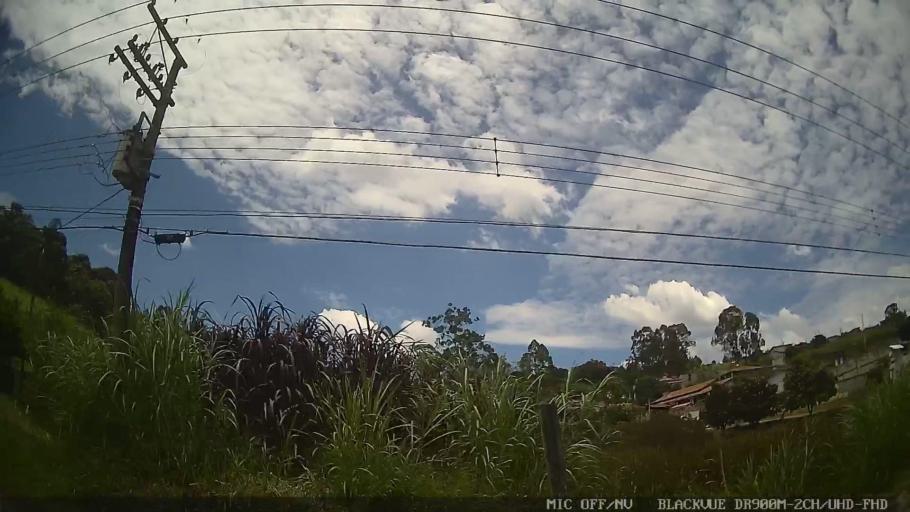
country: BR
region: Sao Paulo
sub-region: Biritiba-Mirim
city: Biritiba Mirim
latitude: -23.5429
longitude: -45.9428
